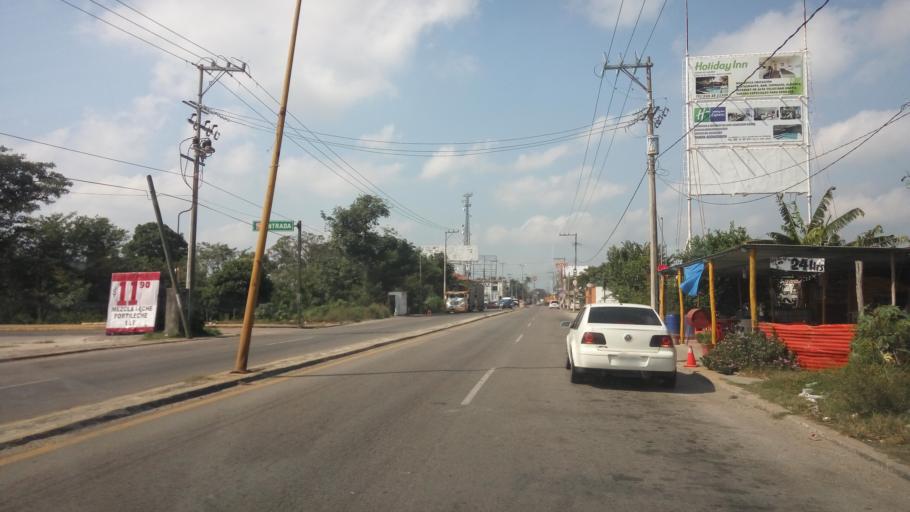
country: MX
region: Tabasco
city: Frontera
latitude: 18.5303
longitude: -92.6366
